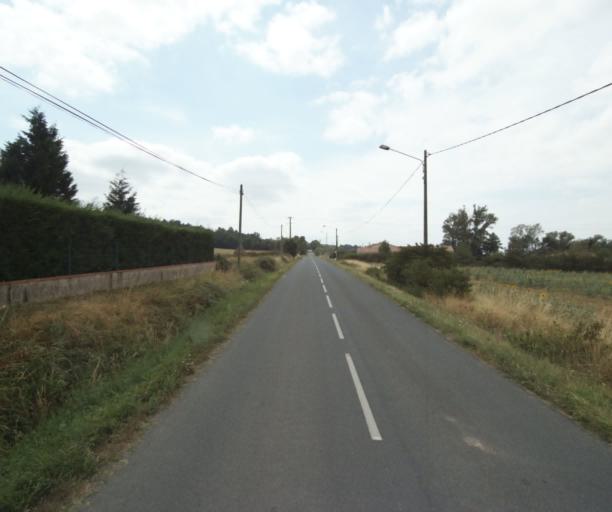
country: FR
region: Midi-Pyrenees
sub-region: Departement de la Haute-Garonne
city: Revel
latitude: 43.4475
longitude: 1.9940
